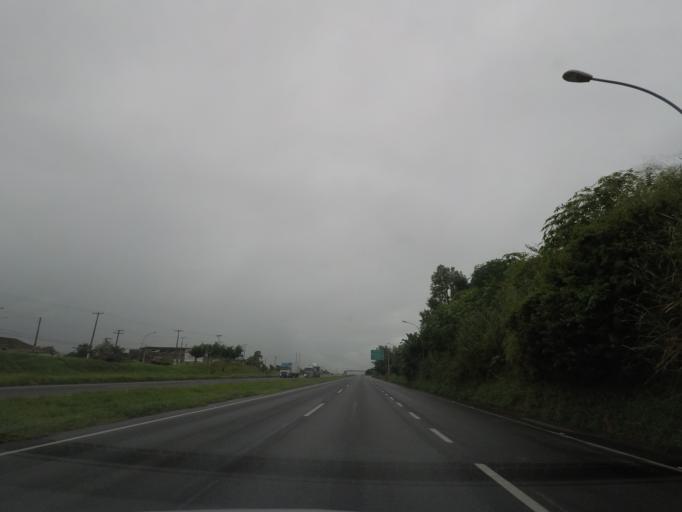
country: BR
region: Sao Paulo
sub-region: Jacupiranga
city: Jacupiranga
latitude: -24.7051
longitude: -48.0123
